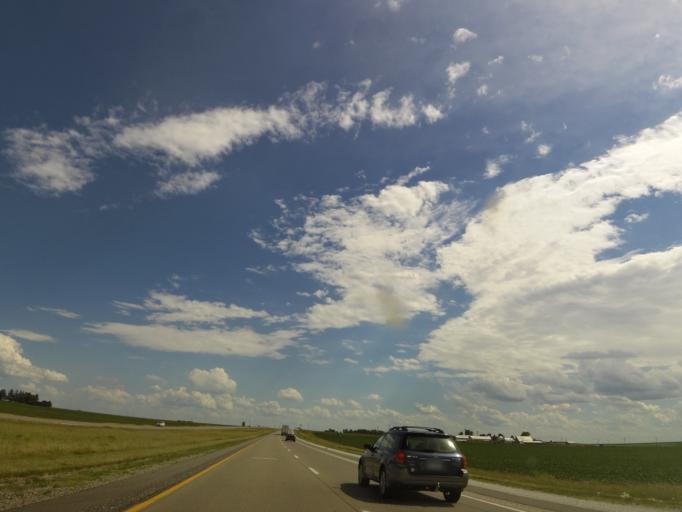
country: US
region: Iowa
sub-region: Henry County
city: Winfield
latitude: 41.1496
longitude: -91.5400
